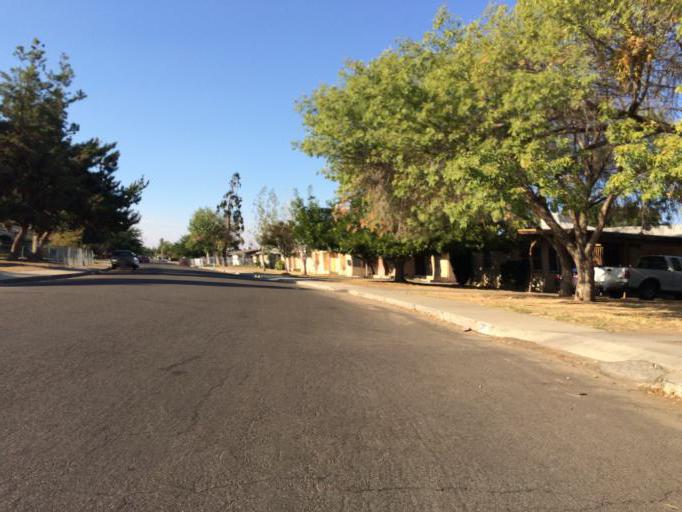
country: US
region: California
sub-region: Fresno County
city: Fresno
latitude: 36.7668
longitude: -119.7645
